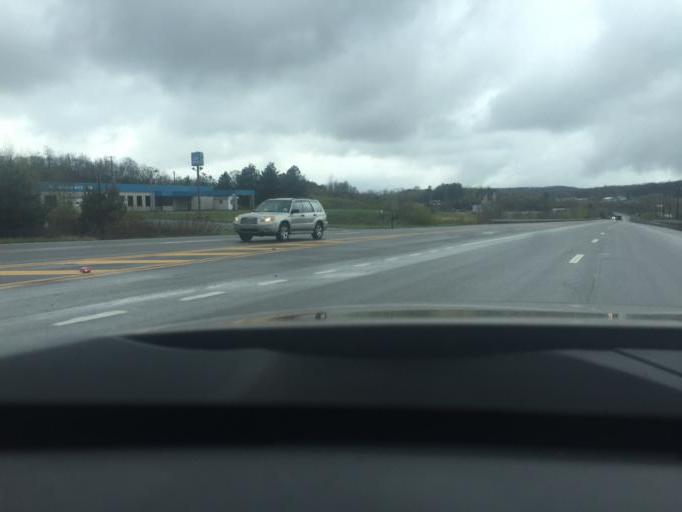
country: US
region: Pennsylvania
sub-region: Luzerne County
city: Harleigh
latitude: 40.9921
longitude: -75.9856
